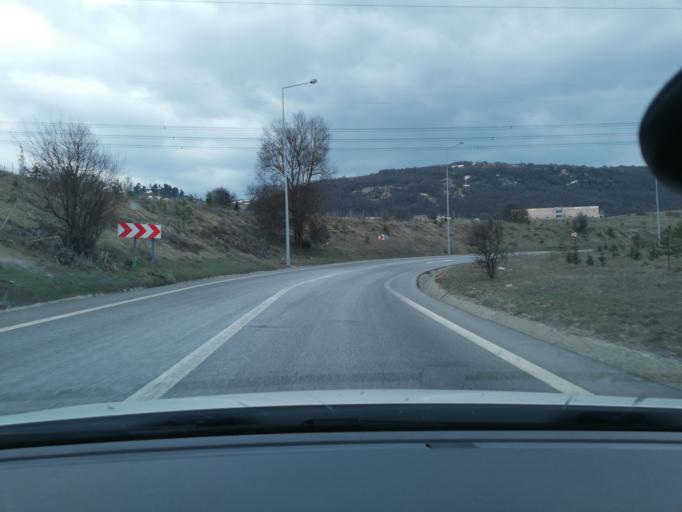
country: TR
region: Bolu
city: Yenicaga
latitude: 40.7632
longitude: 32.0100
